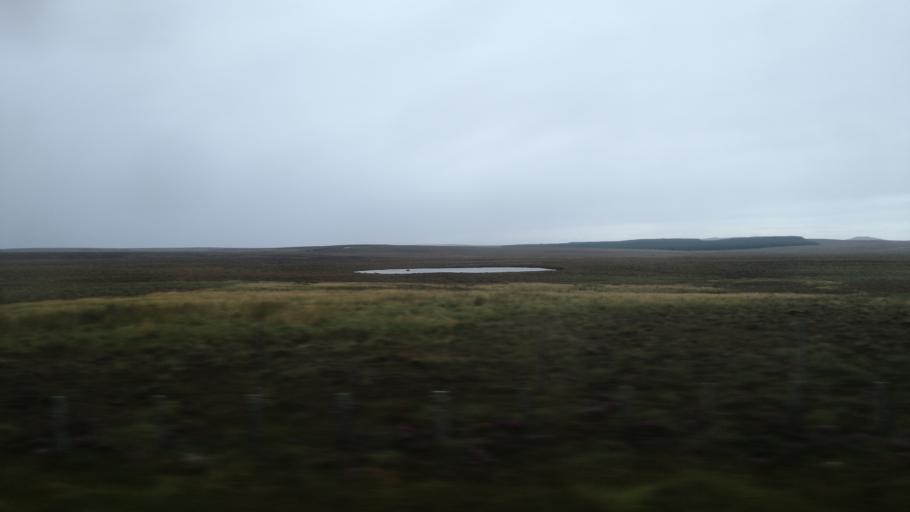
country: GB
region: Scotland
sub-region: Highland
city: Thurso
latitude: 58.3721
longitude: -3.7353
